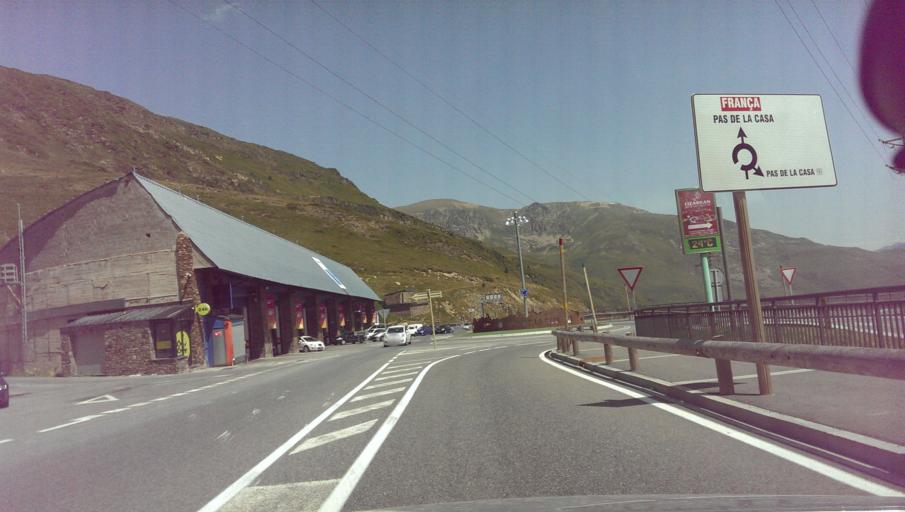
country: AD
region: Encamp
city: Pas de la Casa
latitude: 42.5460
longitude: 1.7308
